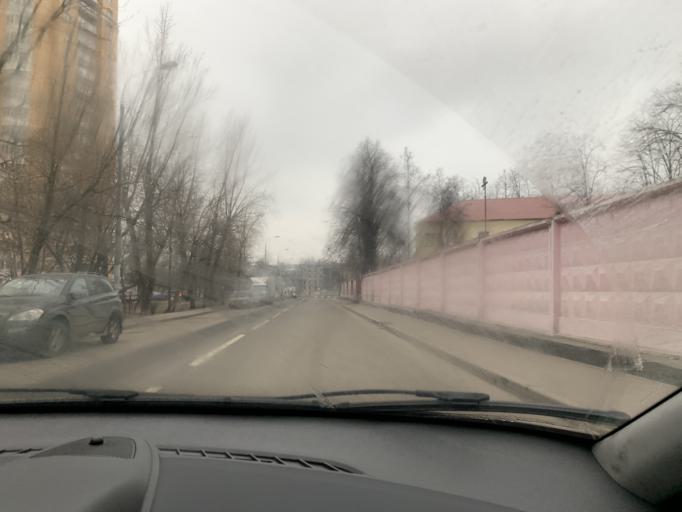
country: RU
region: Moskovskaya
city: Vostochnoe Degunino
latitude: 55.8756
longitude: 37.5500
